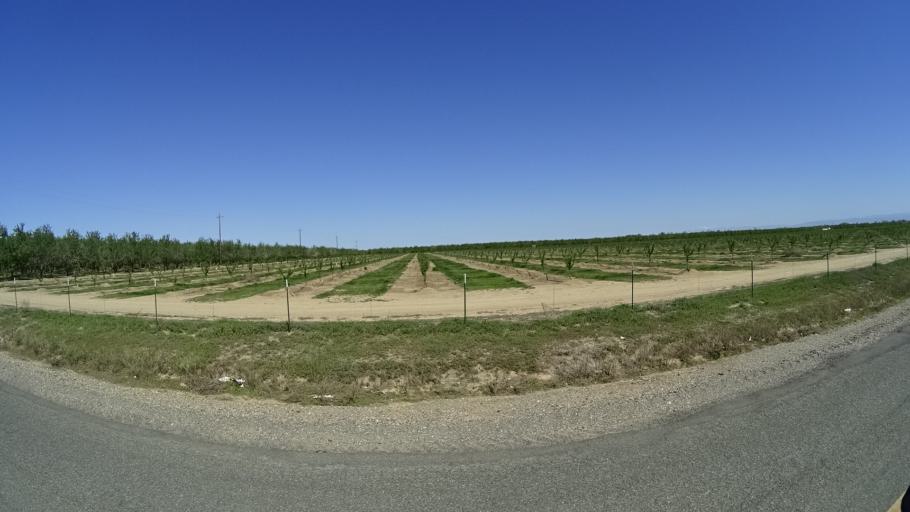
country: US
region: California
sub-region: Glenn County
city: Orland
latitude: 39.6972
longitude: -122.2489
